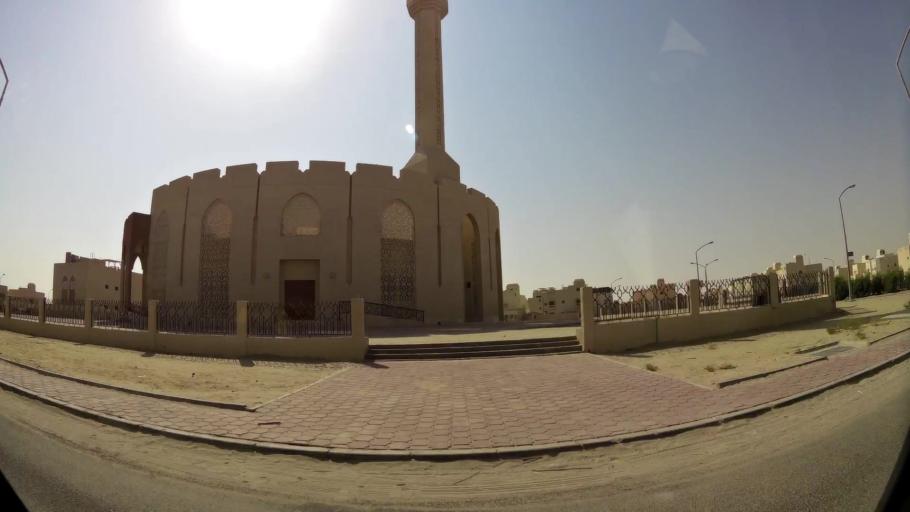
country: KW
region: Al Ahmadi
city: Al Wafrah
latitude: 28.8096
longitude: 48.0576
